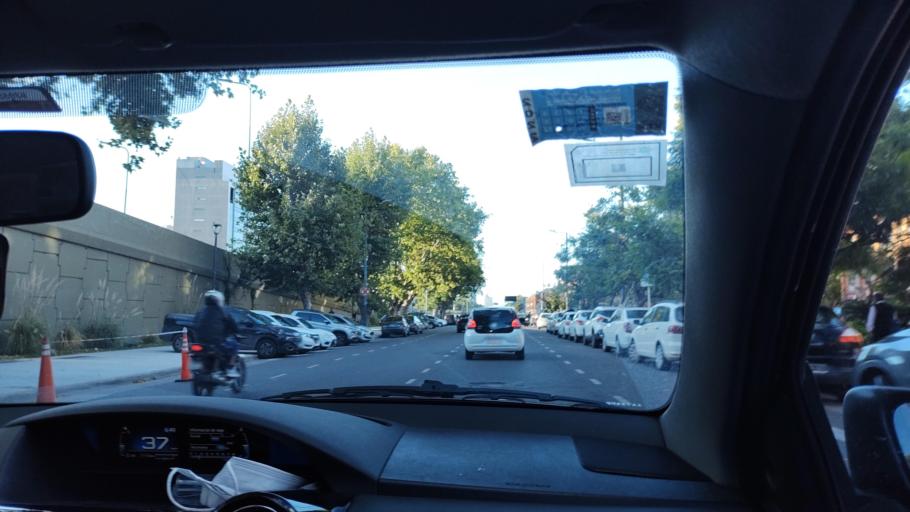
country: AR
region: Buenos Aires F.D.
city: Buenos Aires
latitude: -34.6205
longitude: -58.3654
